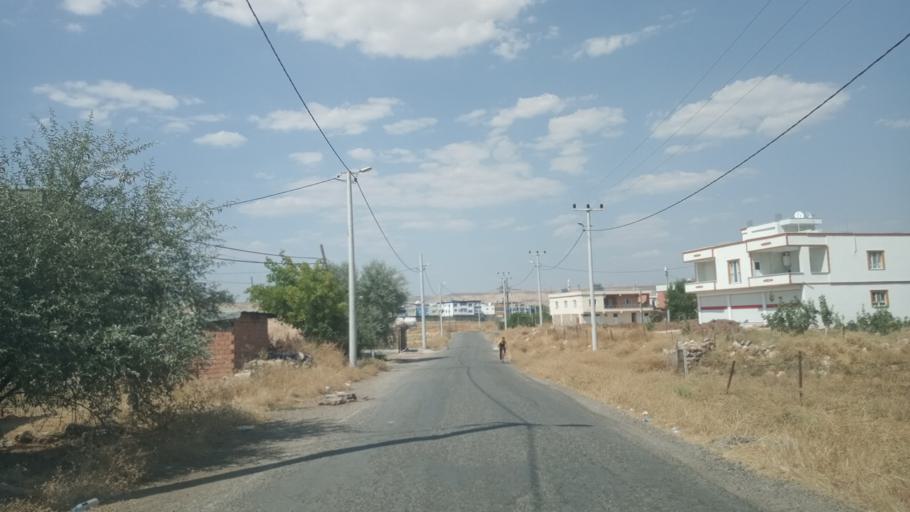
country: TR
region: Batman
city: Binatli
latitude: 37.8424
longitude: 41.2118
